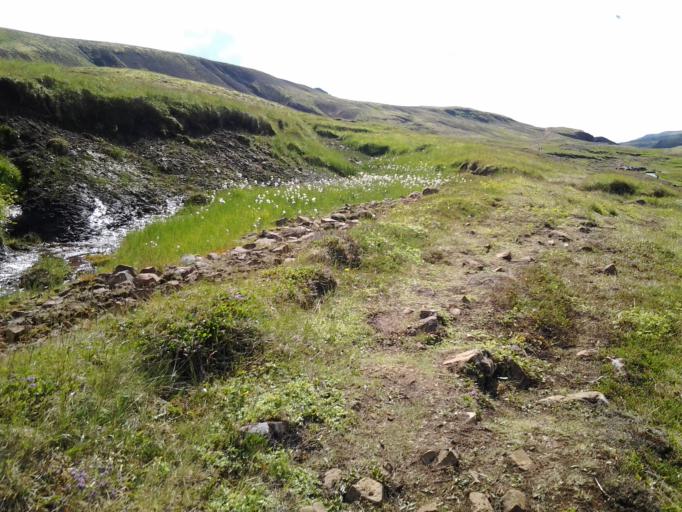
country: IS
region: South
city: Hveragerdi
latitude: 64.0421
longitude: -21.2181
